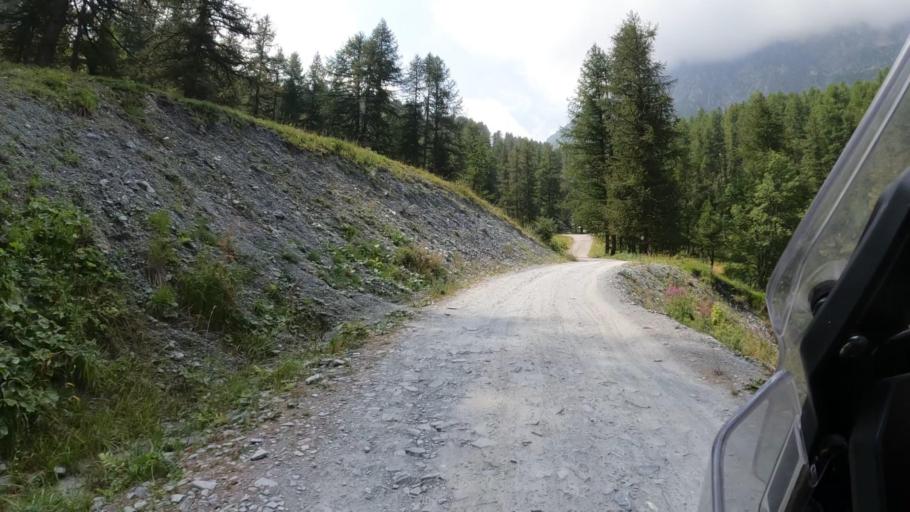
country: IT
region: Piedmont
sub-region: Provincia di Cuneo
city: Marmora
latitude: 44.4188
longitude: 7.1034
